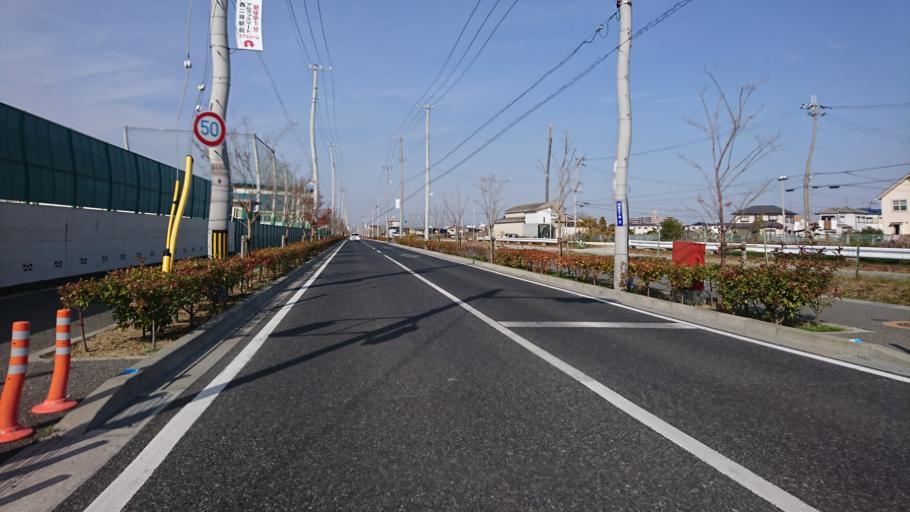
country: JP
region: Hyogo
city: Kakogawacho-honmachi
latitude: 34.7087
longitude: 134.8723
